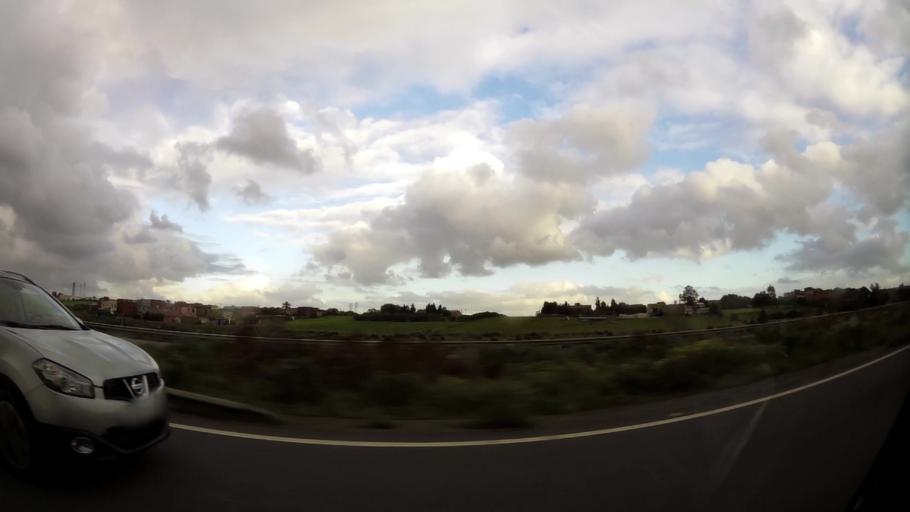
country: MA
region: Grand Casablanca
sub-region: Mohammedia
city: Mohammedia
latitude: 33.6257
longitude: -7.4285
